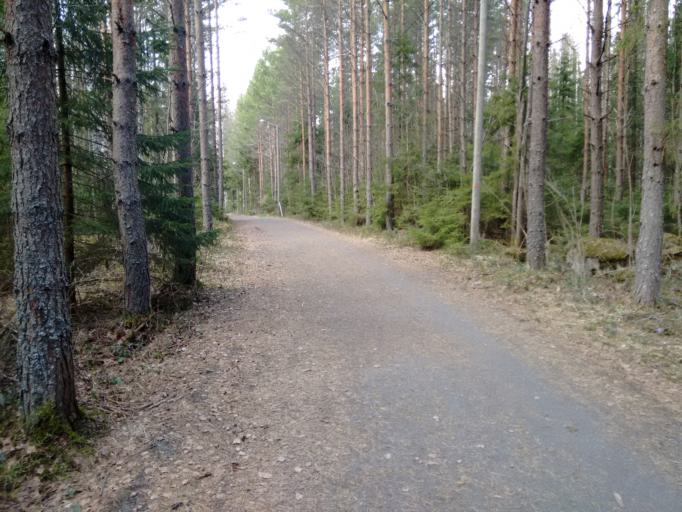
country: FI
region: Pirkanmaa
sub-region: Tampere
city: Tampere
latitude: 61.4437
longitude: 23.8167
